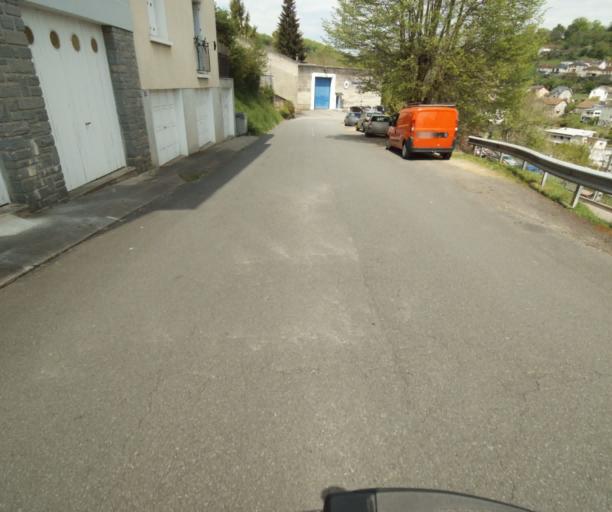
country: FR
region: Limousin
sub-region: Departement de la Correze
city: Tulle
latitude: 45.2745
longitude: 1.7694
